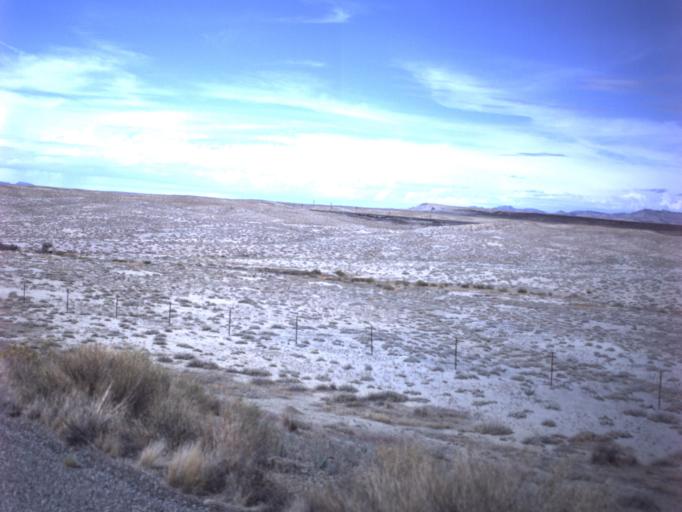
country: US
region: Utah
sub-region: Grand County
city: Moab
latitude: 38.9395
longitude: -109.4099
